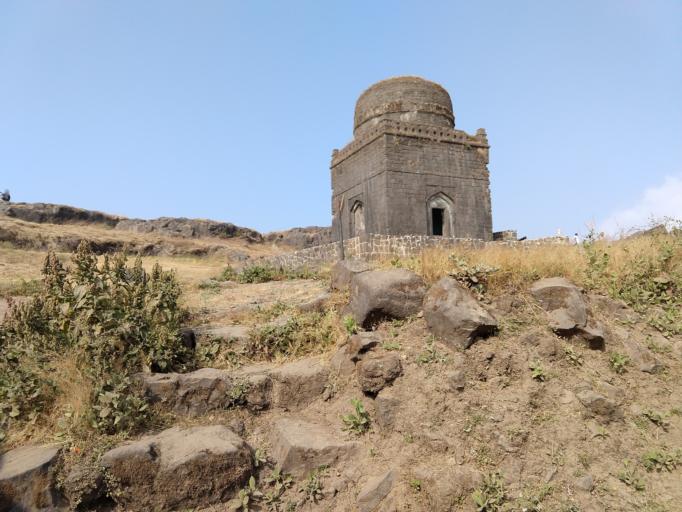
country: IN
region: Maharashtra
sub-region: Pune Division
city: Lonavla
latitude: 18.7074
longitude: 73.4775
